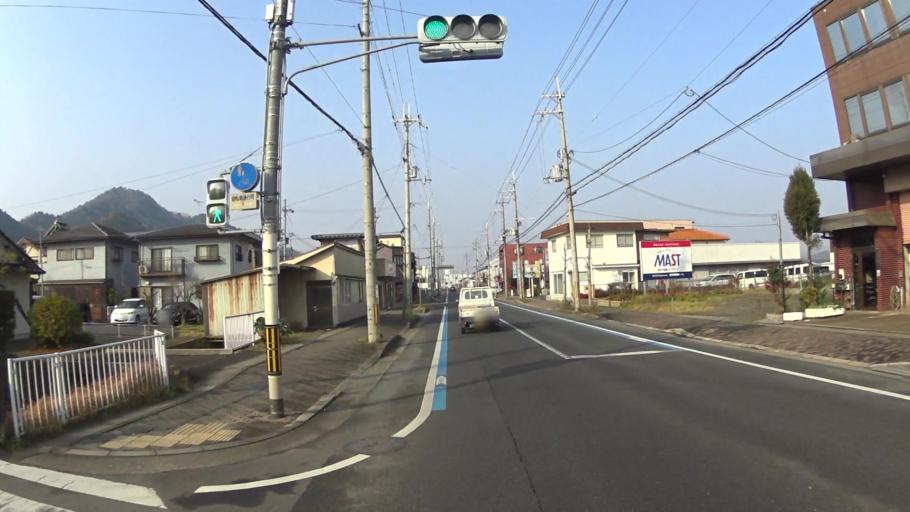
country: JP
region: Kyoto
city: Ayabe
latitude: 35.3024
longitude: 135.2376
